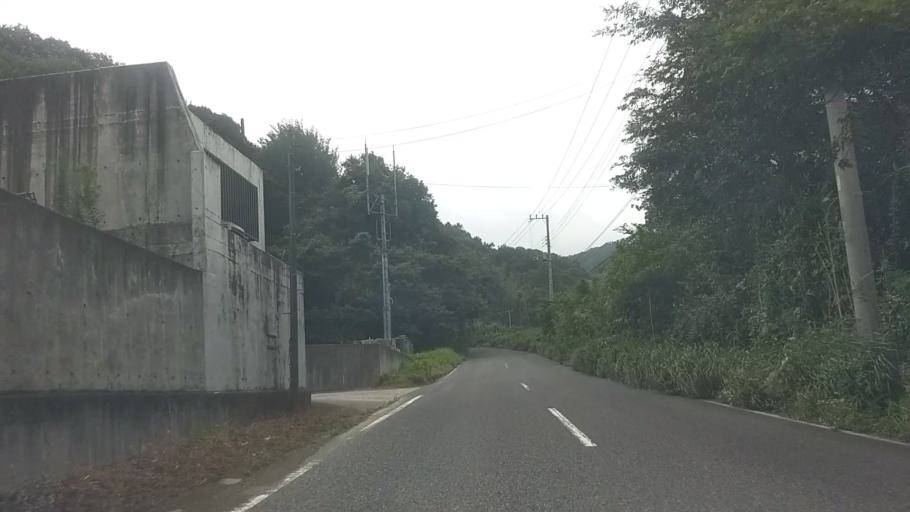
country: JP
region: Chiba
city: Kimitsu
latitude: 35.2381
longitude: 139.9870
